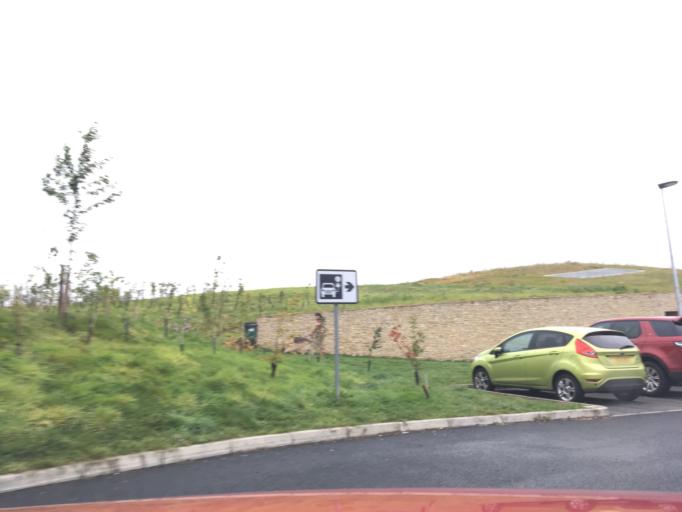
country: GB
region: England
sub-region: Gloucestershire
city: Painswick
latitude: 51.8182
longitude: -2.2225
